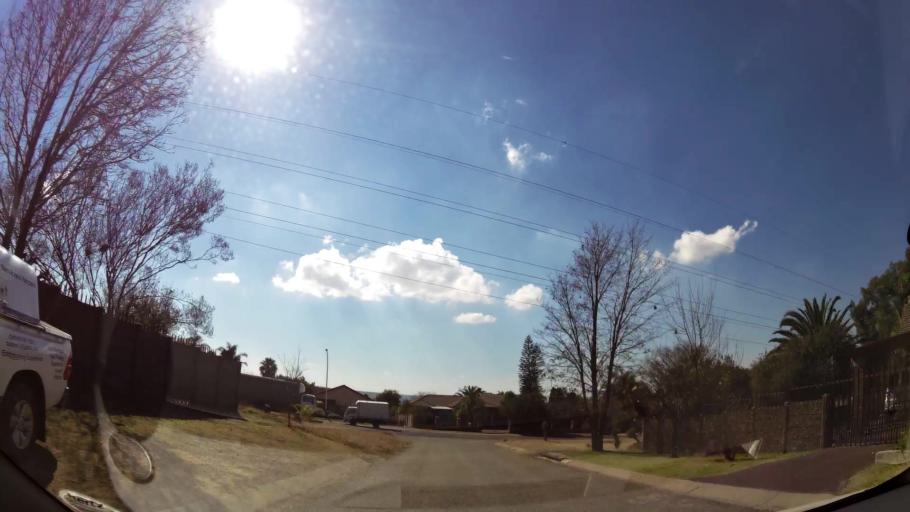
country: ZA
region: Mpumalanga
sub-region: Nkangala District Municipality
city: Witbank
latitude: -25.8574
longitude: 29.2429
